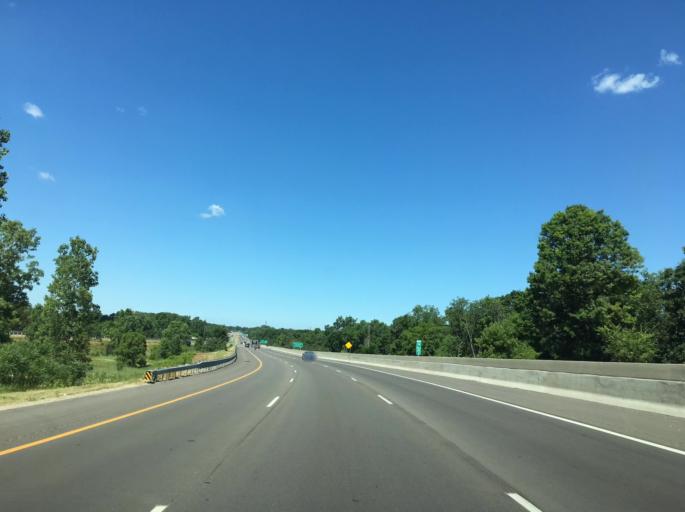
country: US
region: Michigan
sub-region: Oakland County
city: Clarkston
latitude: 42.7454
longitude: -83.3954
